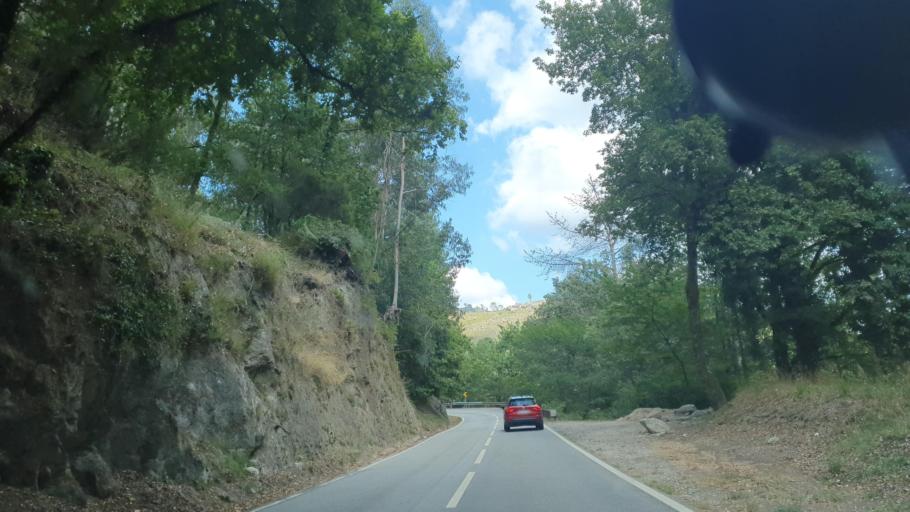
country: PT
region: Braga
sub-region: Vieira do Minho
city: Real
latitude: 41.7116
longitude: -8.2198
